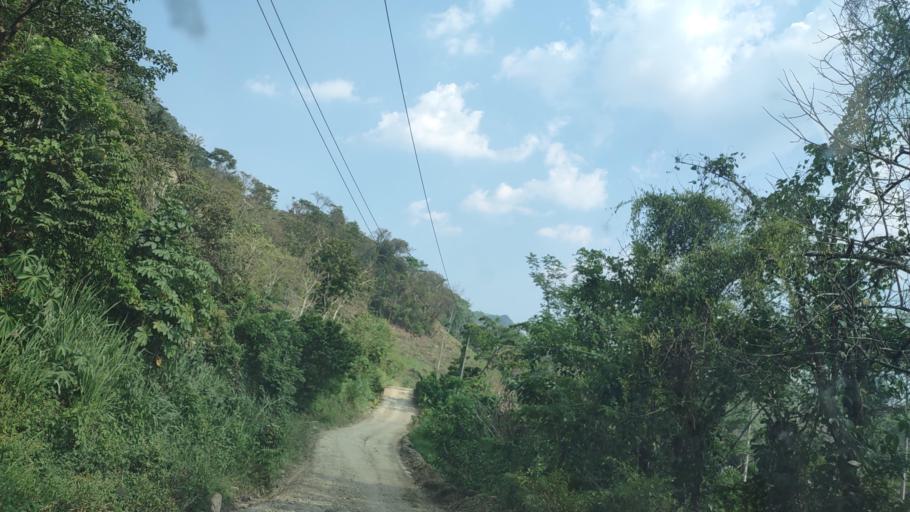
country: MX
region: Chiapas
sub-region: Tecpatan
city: Raudales Malpaso
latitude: 17.3204
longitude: -93.7419
